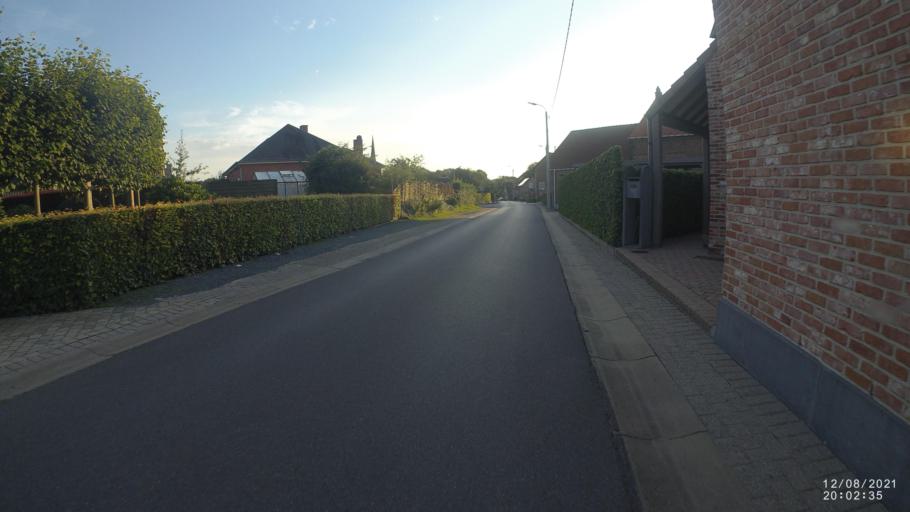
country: BE
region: Flanders
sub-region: Provincie Vlaams-Brabant
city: Dilbeek
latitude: 50.8639
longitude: 4.2177
